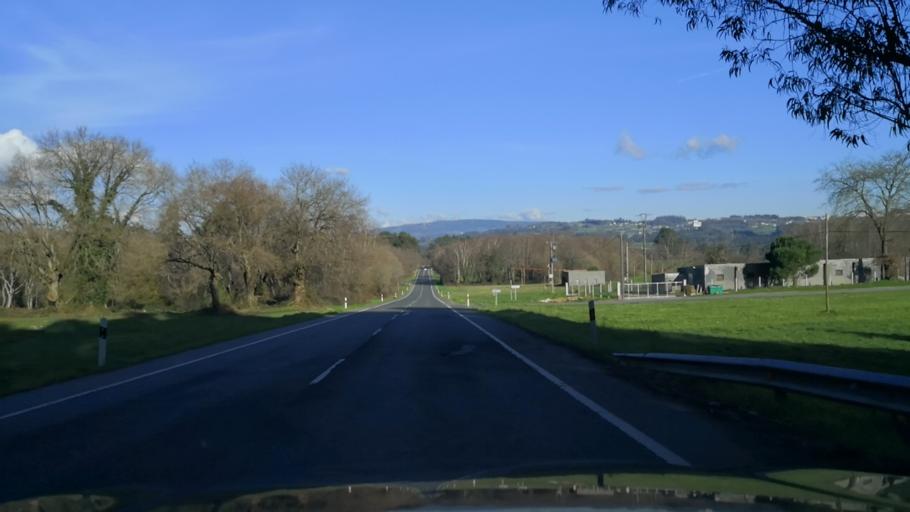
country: ES
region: Galicia
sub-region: Provincia de Pontevedra
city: Silleda
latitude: 42.7057
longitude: -8.3056
